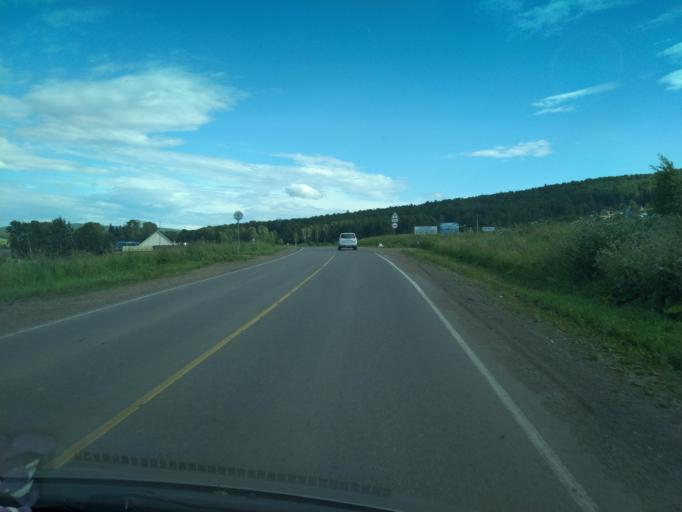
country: RU
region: Krasnoyarskiy
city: Zykovo
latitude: 55.8765
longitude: 93.2248
